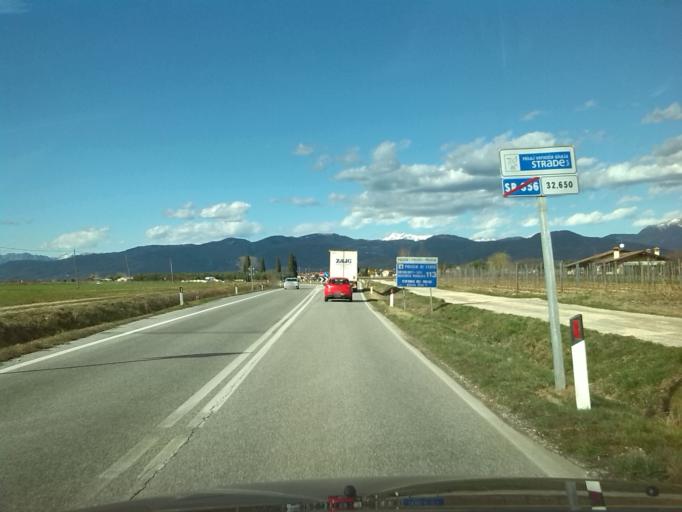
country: IT
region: Friuli Venezia Giulia
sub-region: Provincia di Udine
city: Cividale del Friuli
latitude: 46.0634
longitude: 13.4346
